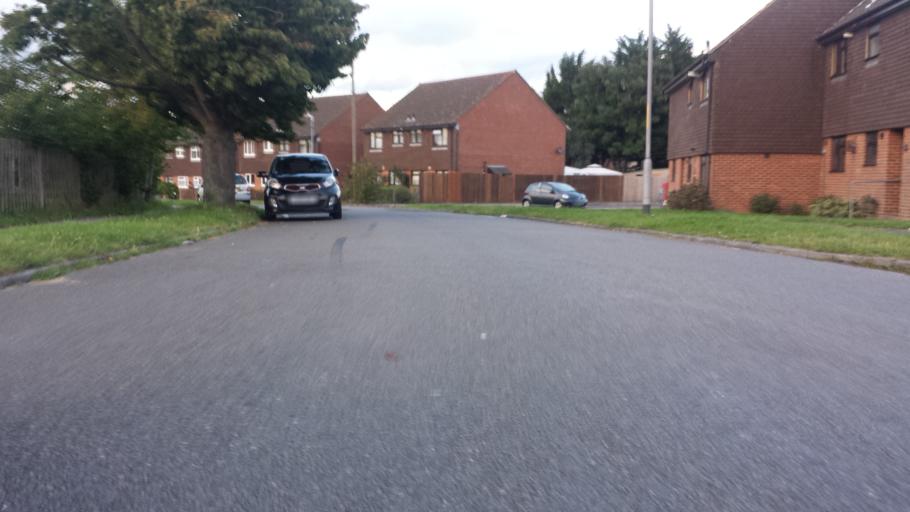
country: GB
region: England
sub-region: Kent
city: Swanley
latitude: 51.3947
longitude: 0.1651
